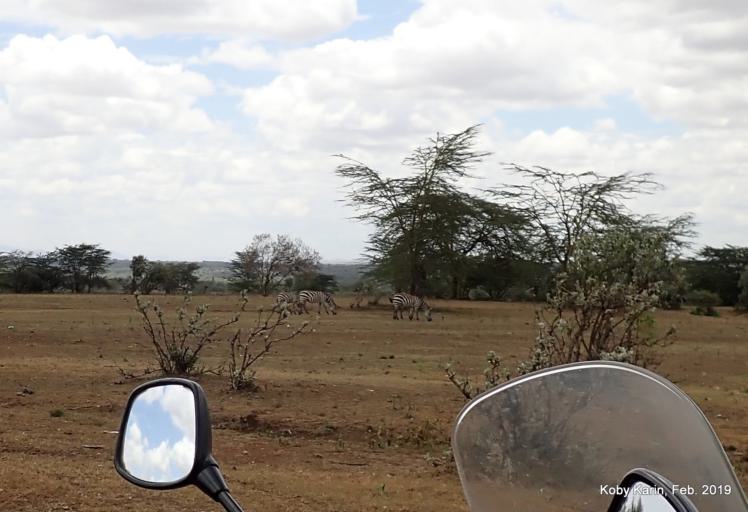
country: KE
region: Narok
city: Narok
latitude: -1.0324
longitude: 35.7067
